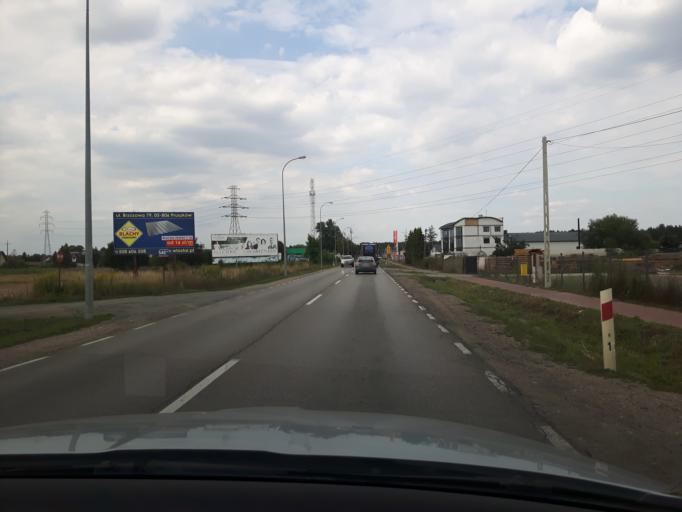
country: PL
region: Masovian Voivodeship
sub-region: Powiat legionowski
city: Stanislawow Pierwszy
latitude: 52.3732
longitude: 21.0290
